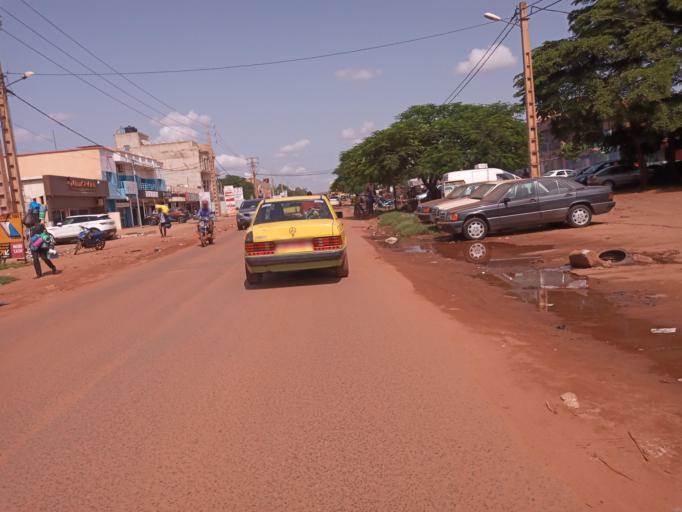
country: ML
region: Bamako
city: Bamako
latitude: 12.5971
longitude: -8.0222
